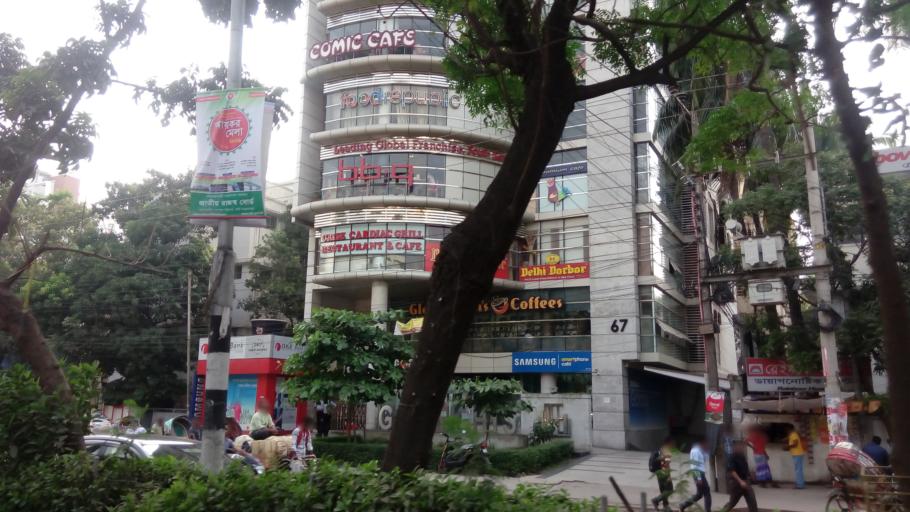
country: BD
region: Dhaka
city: Azimpur
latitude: 23.7500
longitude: 90.3688
